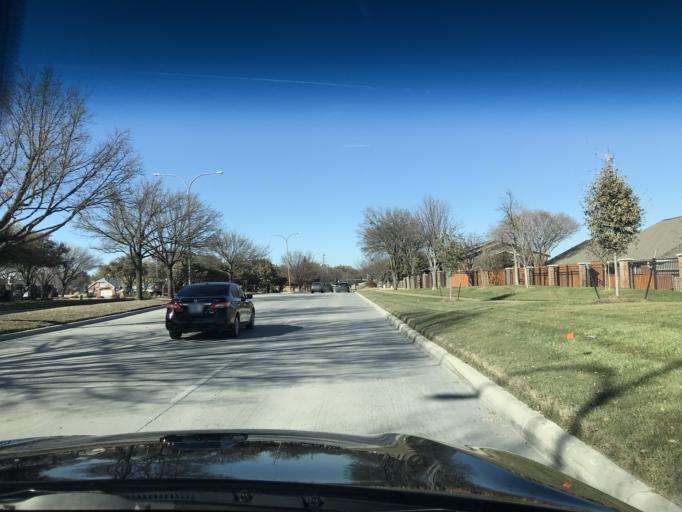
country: US
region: Texas
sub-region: Tarrant County
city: Benbrook
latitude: 32.6695
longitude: -97.4192
